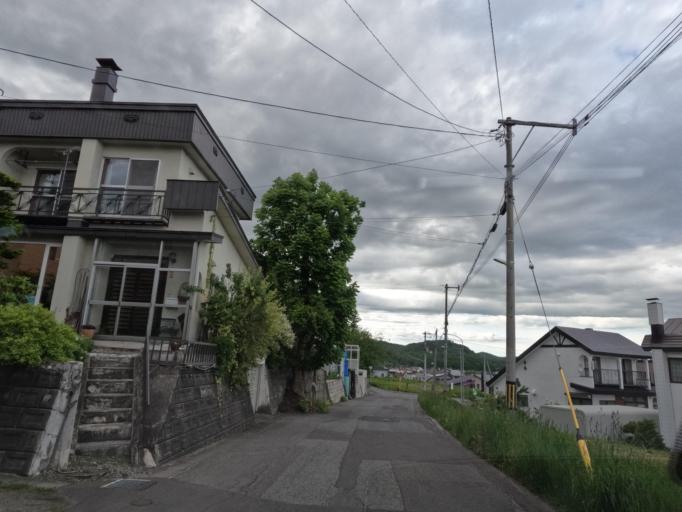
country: JP
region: Hokkaido
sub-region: Asahikawa-shi
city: Asahikawa
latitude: 43.7710
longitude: 142.3115
